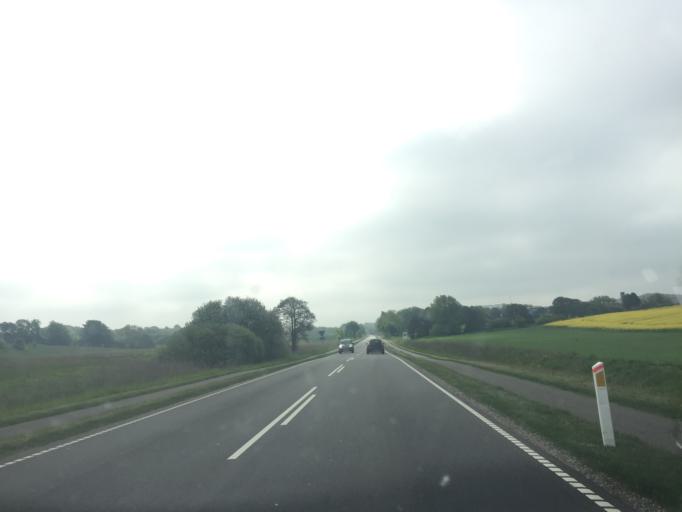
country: DK
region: South Denmark
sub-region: Kolding Kommune
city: Sonder Bjert
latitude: 55.4702
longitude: 9.5298
